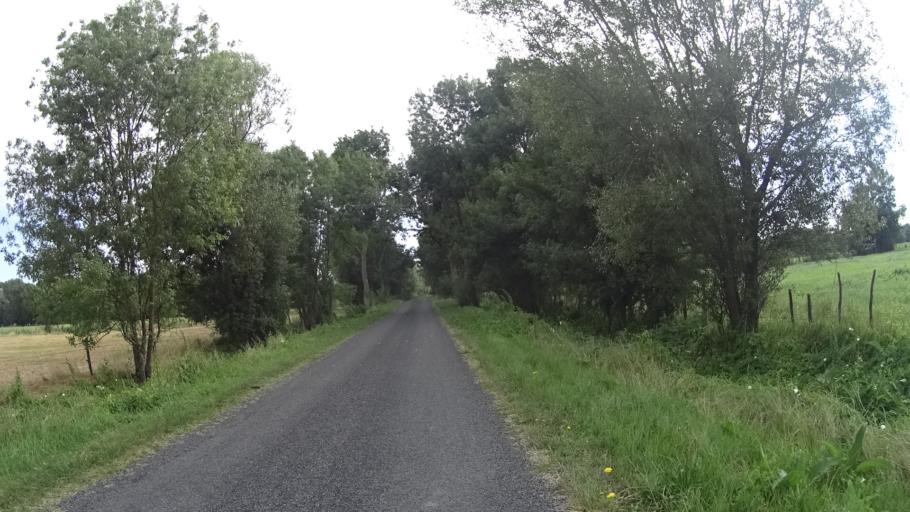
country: FR
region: Centre
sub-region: Departement d'Indre-et-Loire
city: Chouze-sur-Loire
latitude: 47.2071
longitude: 0.1109
